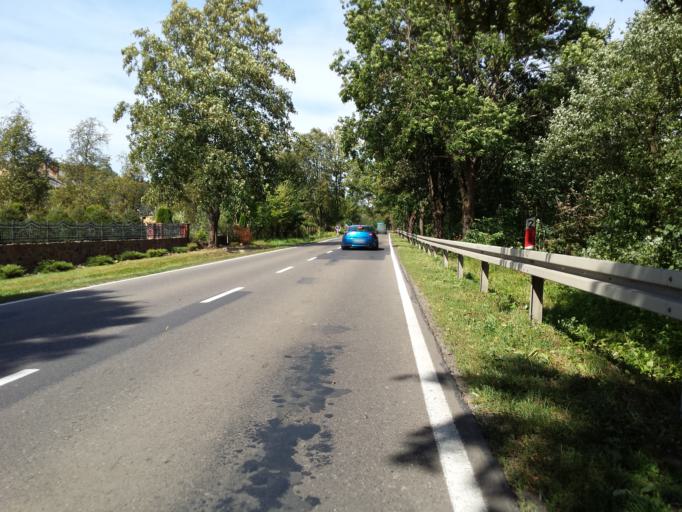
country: PL
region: Subcarpathian Voivodeship
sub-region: Powiat leski
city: Lesko
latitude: 49.4602
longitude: 22.3341
